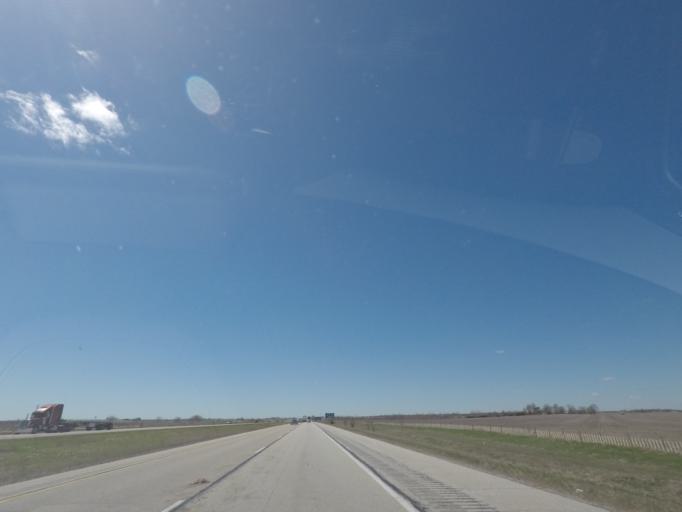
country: US
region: Illinois
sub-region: McLean County
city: Normal
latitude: 40.5537
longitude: -88.9161
